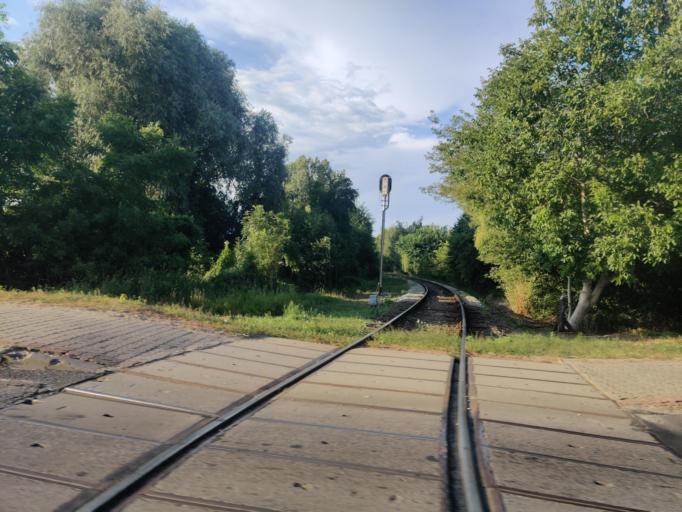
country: PL
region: Greater Poland Voivodeship
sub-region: Konin
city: Konin
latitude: 52.2356
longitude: 18.2679
